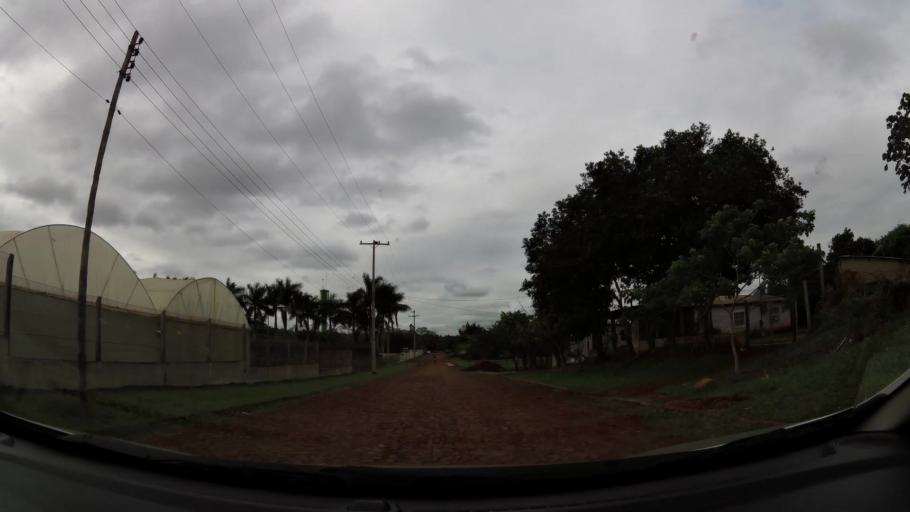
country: PY
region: Alto Parana
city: Ciudad del Este
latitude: -25.4028
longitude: -54.6357
